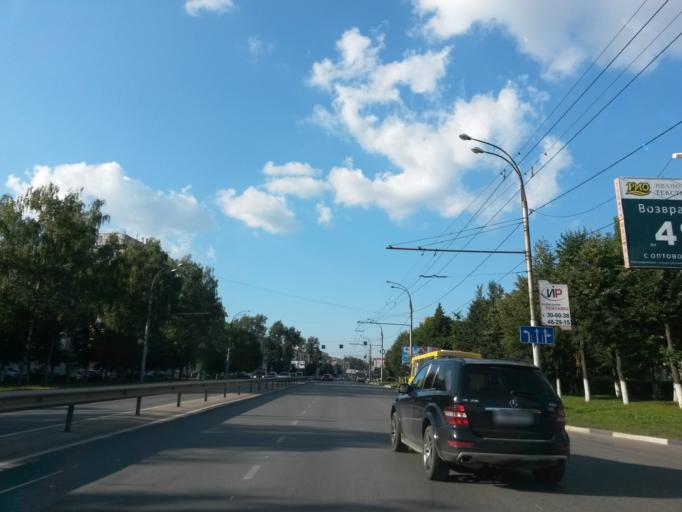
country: RU
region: Ivanovo
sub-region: Gorod Ivanovo
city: Ivanovo
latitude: 56.9674
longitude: 40.9735
